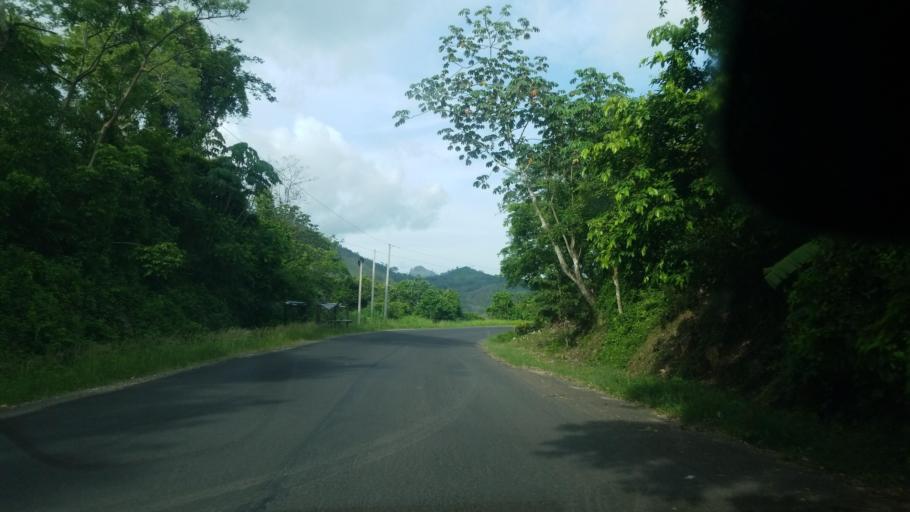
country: HN
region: Santa Barbara
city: Trinidad
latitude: 15.1779
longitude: -88.2698
